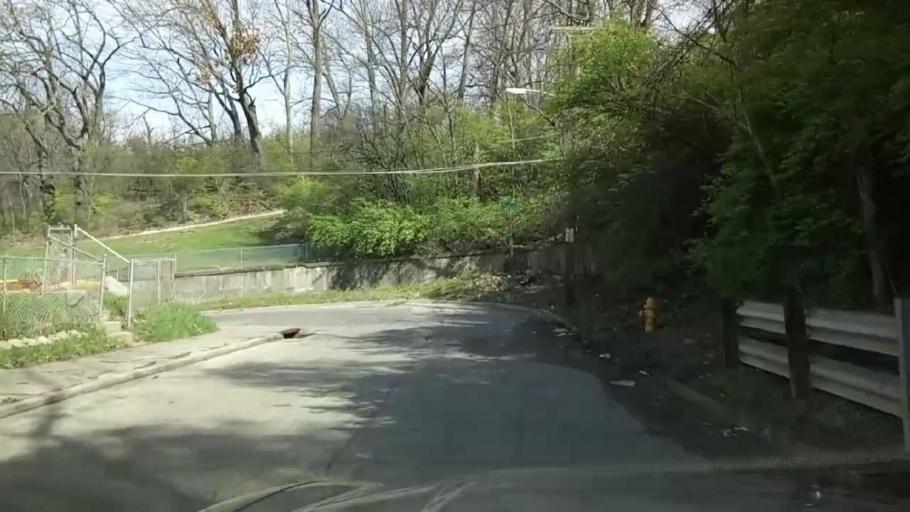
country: US
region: Kentucky
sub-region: Campbell County
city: Newport
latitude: 39.1231
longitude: -84.5132
